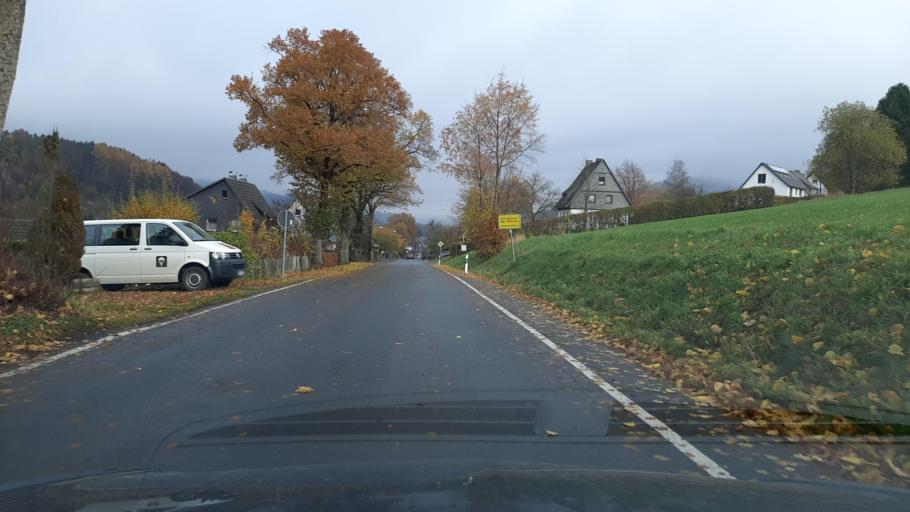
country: DE
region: North Rhine-Westphalia
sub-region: Regierungsbezirk Arnsberg
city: Winterberg
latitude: 51.2448
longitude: 8.4689
